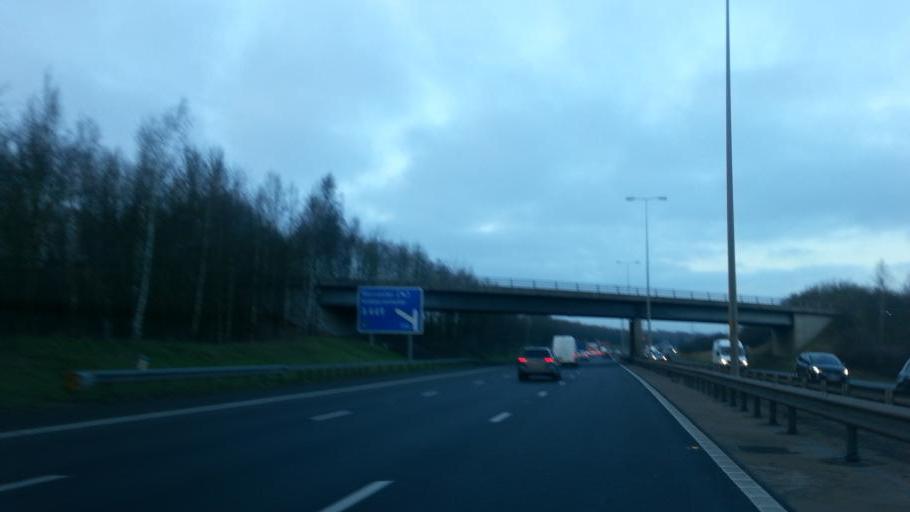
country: GB
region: England
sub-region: Worcestershire
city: Fernhill Heath
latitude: 52.1930
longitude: -2.1680
